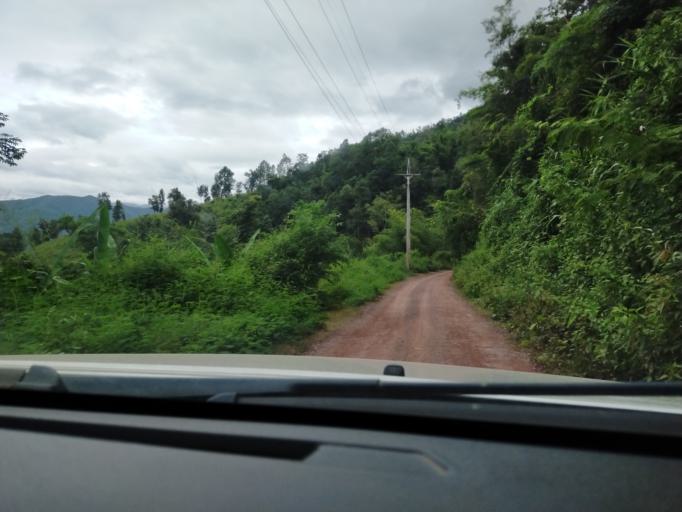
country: TH
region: Nan
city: Chaloem Phra Kiat
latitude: 19.7804
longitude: 101.3603
